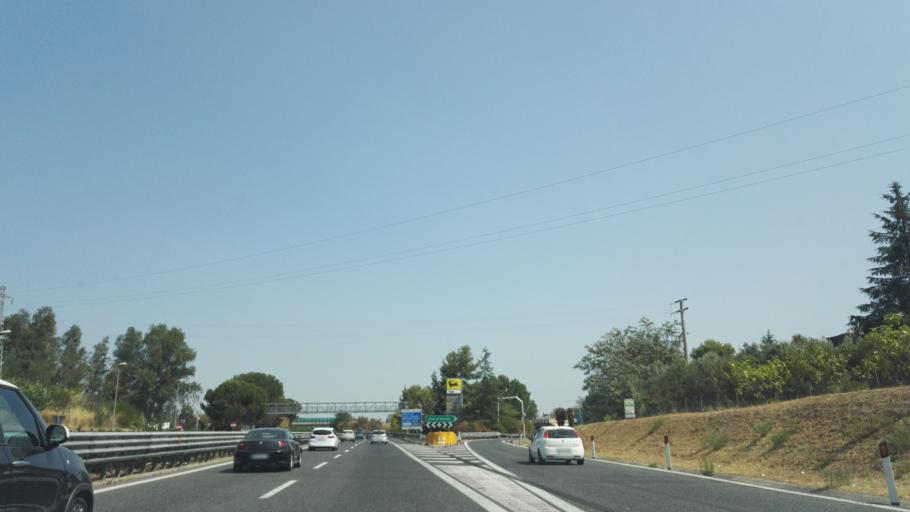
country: IT
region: Calabria
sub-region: Provincia di Cosenza
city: Quattromiglia
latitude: 39.3431
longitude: 16.2348
